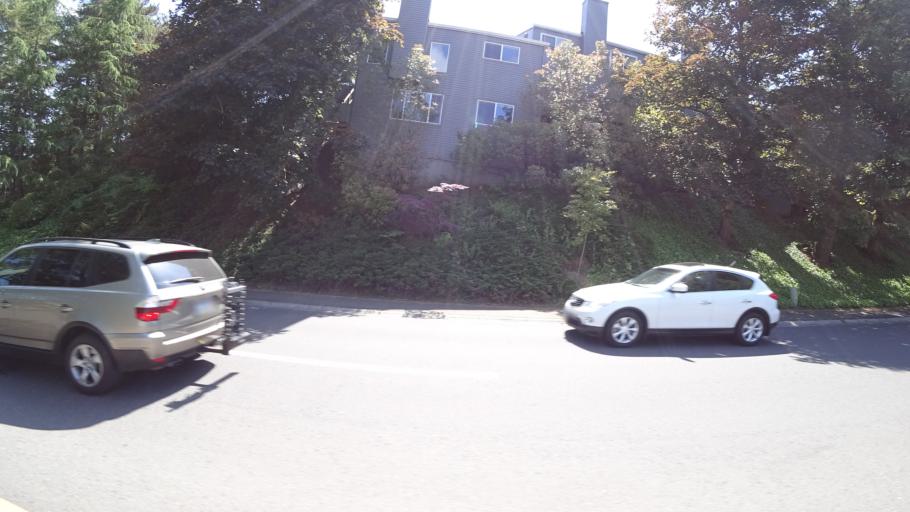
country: US
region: Oregon
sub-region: Clackamas County
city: Lake Oswego
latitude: 45.4326
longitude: -122.7041
